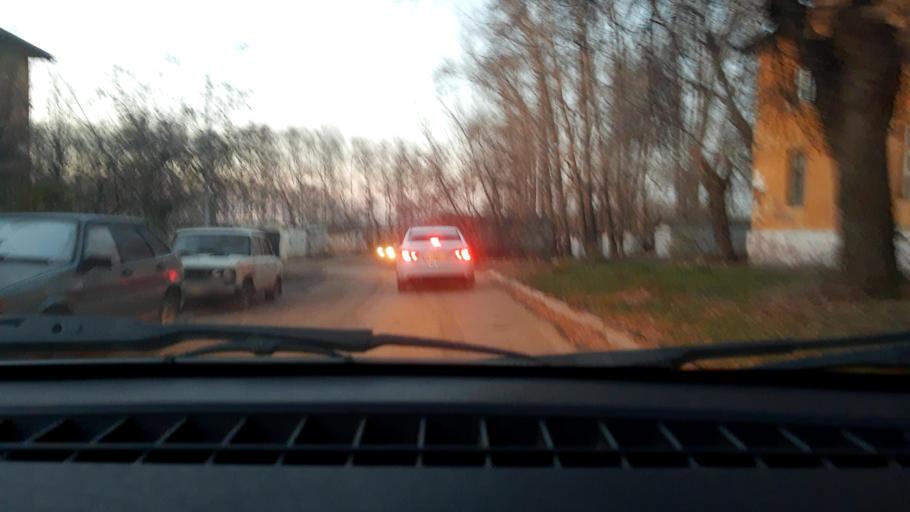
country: RU
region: Bashkortostan
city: Ufa
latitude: 54.8123
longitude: 56.0762
